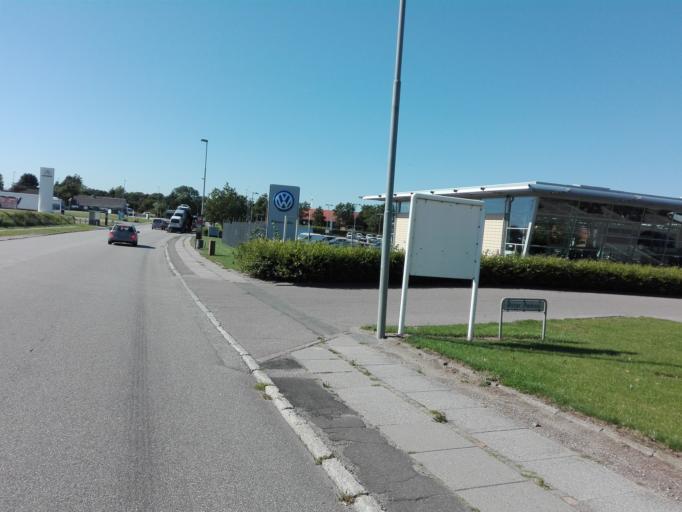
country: DK
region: Central Jutland
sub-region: Arhus Kommune
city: Tranbjerg
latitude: 56.1038
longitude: 10.1480
